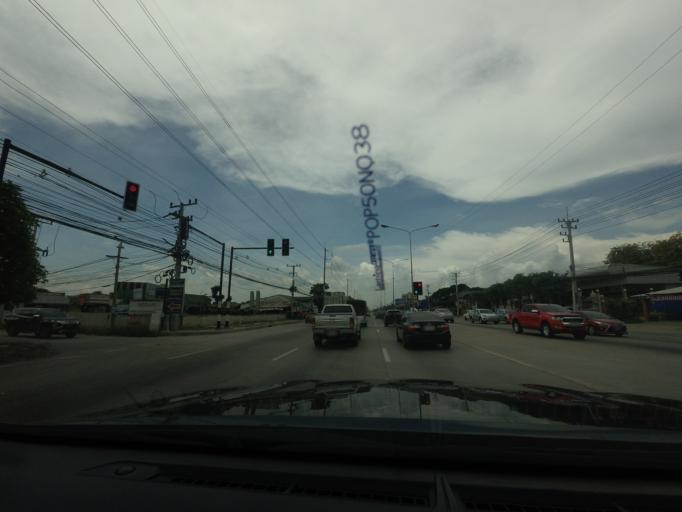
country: TH
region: Nakhon Pathom
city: Nakhon Pathom
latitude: 13.8446
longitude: 100.0246
